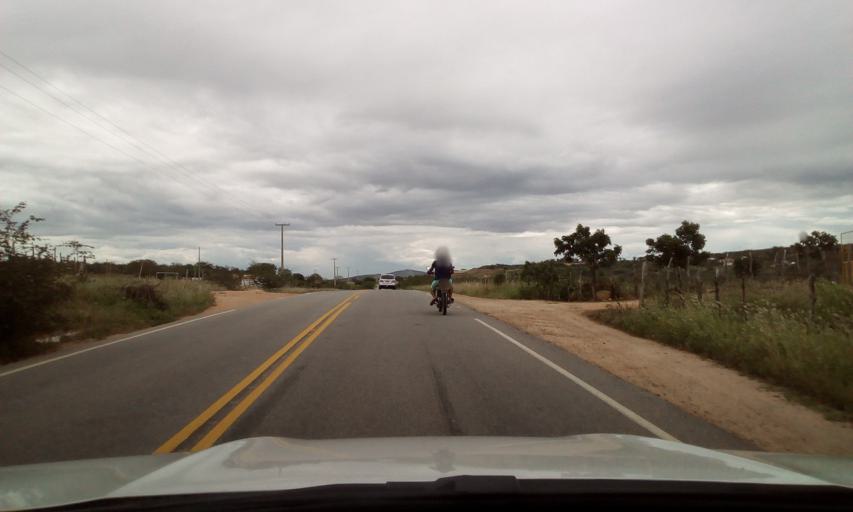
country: BR
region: Paraiba
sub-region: Picui
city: Picui
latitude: -6.5535
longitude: -36.2952
